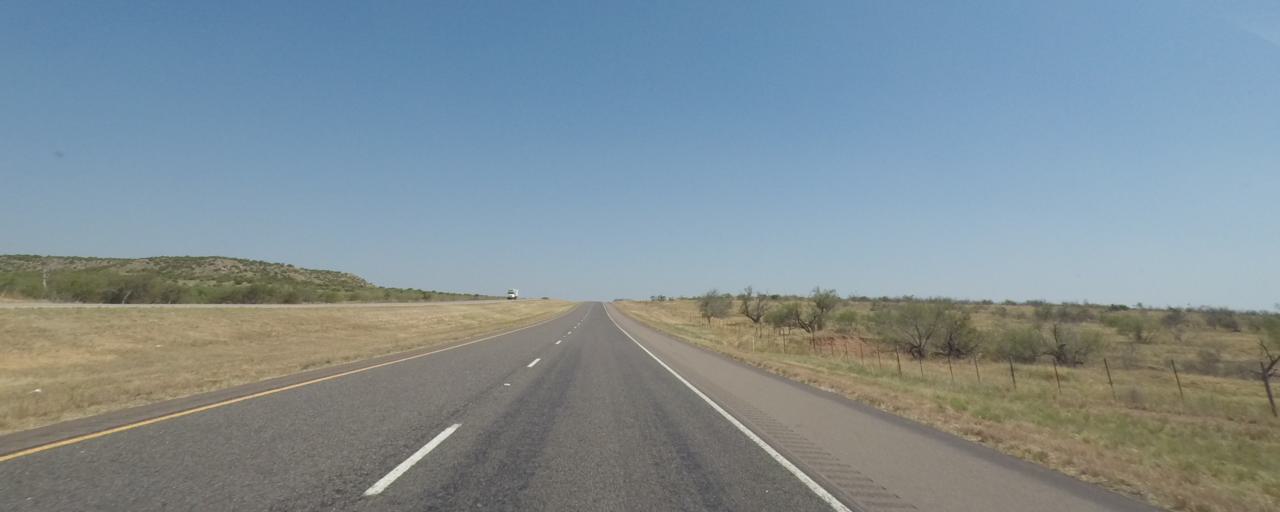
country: US
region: Texas
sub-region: Dickens County
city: Dickens
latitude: 33.6315
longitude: -100.8772
